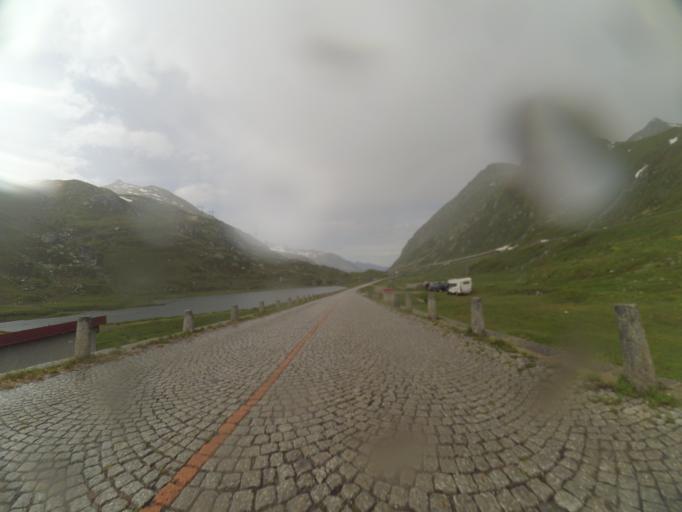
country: CH
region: Ticino
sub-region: Leventina District
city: Airolo
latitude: 46.5695
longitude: 8.5573
